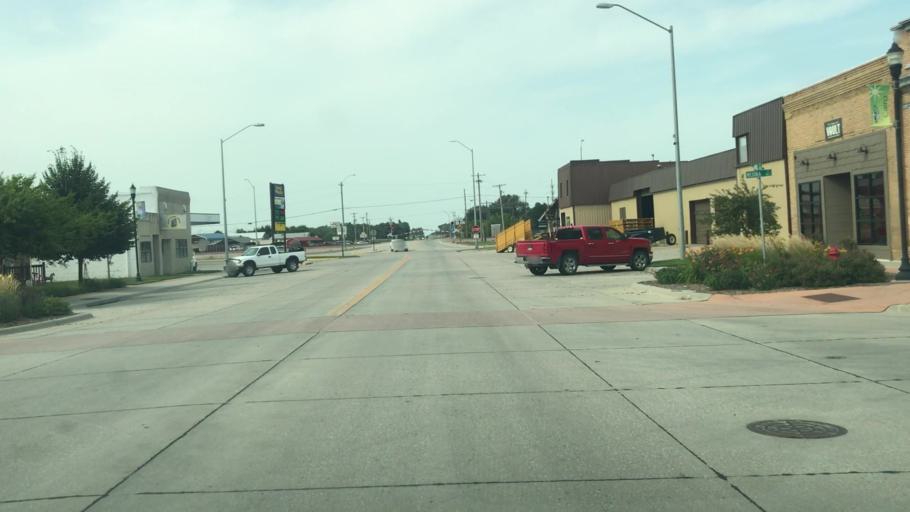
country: US
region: Nebraska
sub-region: Hall County
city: Wood River
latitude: 41.0009
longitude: -98.6074
